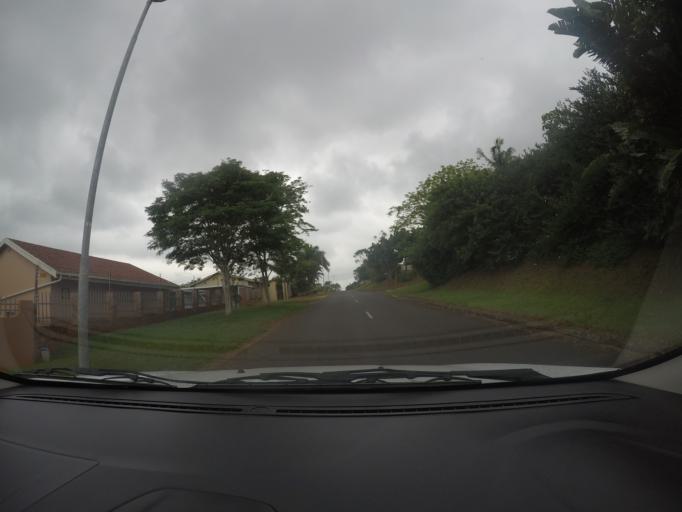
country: ZA
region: KwaZulu-Natal
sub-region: uThungulu District Municipality
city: Empangeni
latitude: -28.7656
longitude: 31.9021
